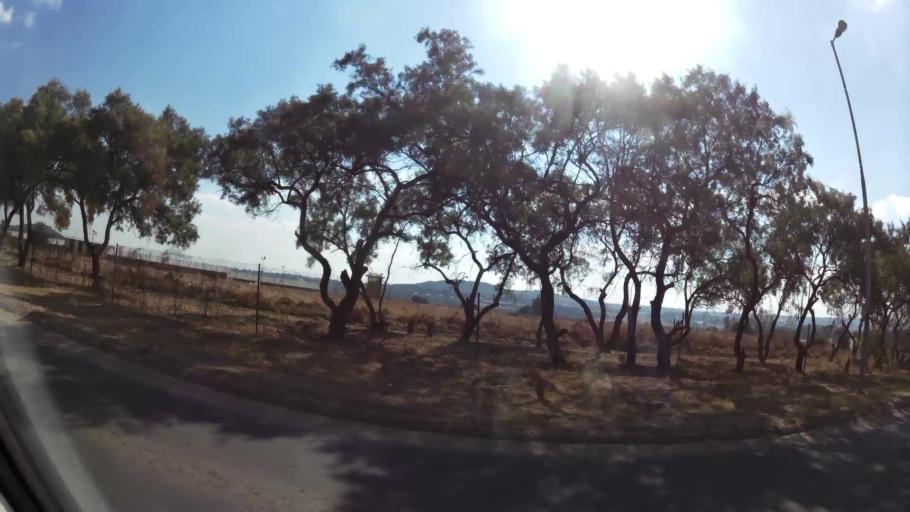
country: ZA
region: Gauteng
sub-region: City of Johannesburg Metropolitan Municipality
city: Midrand
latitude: -26.0199
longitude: 28.0650
